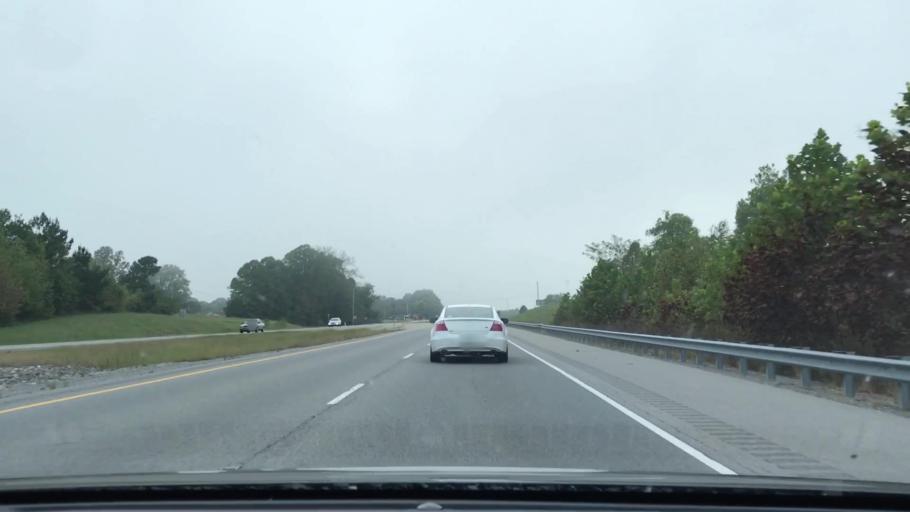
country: US
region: Tennessee
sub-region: Sumner County
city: Portland
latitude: 36.4874
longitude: -86.4877
